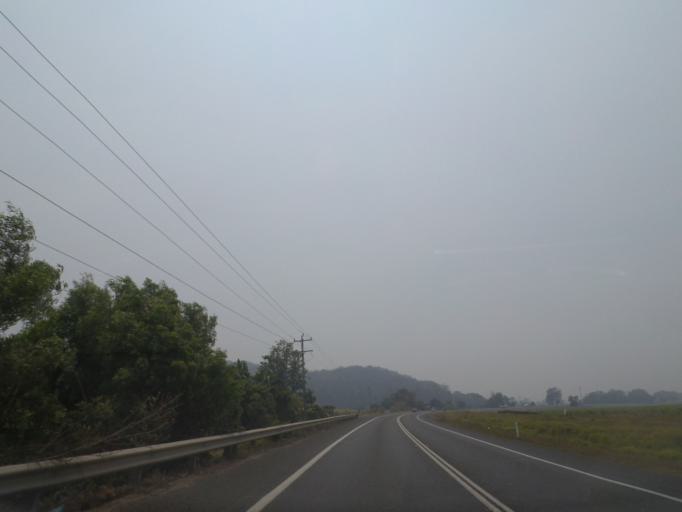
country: AU
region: New South Wales
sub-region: Clarence Valley
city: Maclean
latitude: -29.5424
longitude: 153.1571
